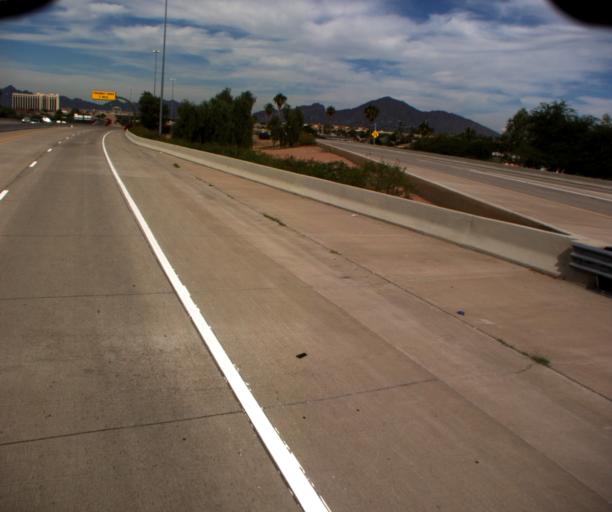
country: US
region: Arizona
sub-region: Maricopa County
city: Tempe Junction
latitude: 33.4496
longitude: -111.9822
